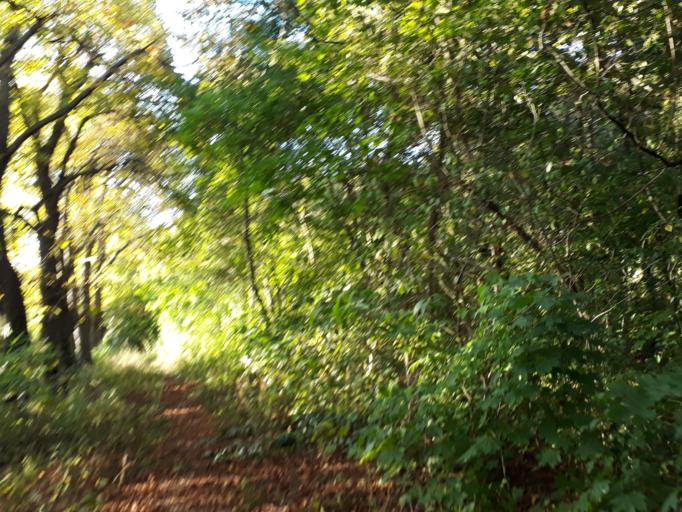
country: HU
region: Budapest
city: Budapest XI. keruelet
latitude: 47.4560
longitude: 19.0050
